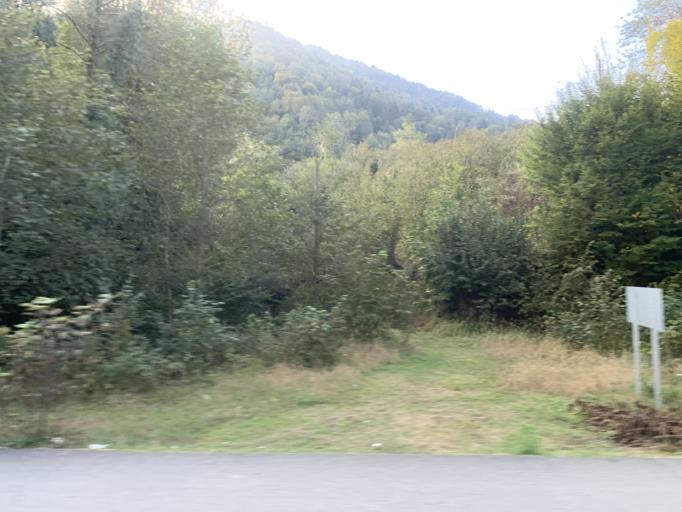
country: TR
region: Trabzon
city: Dernekpazari
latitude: 40.8471
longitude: 40.2812
